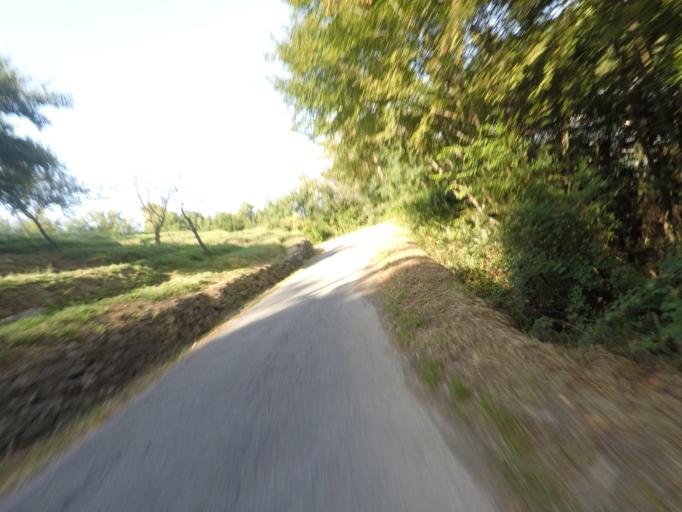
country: IT
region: Tuscany
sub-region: Provincia di Massa-Carrara
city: Carrara
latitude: 44.0789
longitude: 10.0660
